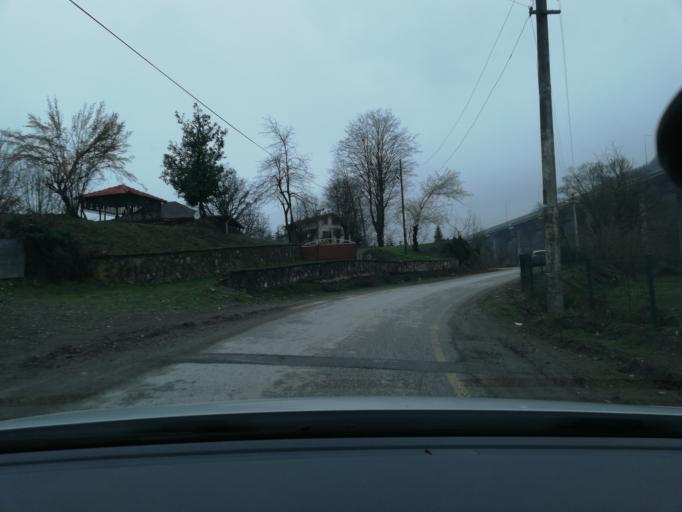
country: TR
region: Duzce
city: Kaynasli
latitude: 40.7698
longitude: 31.3627
